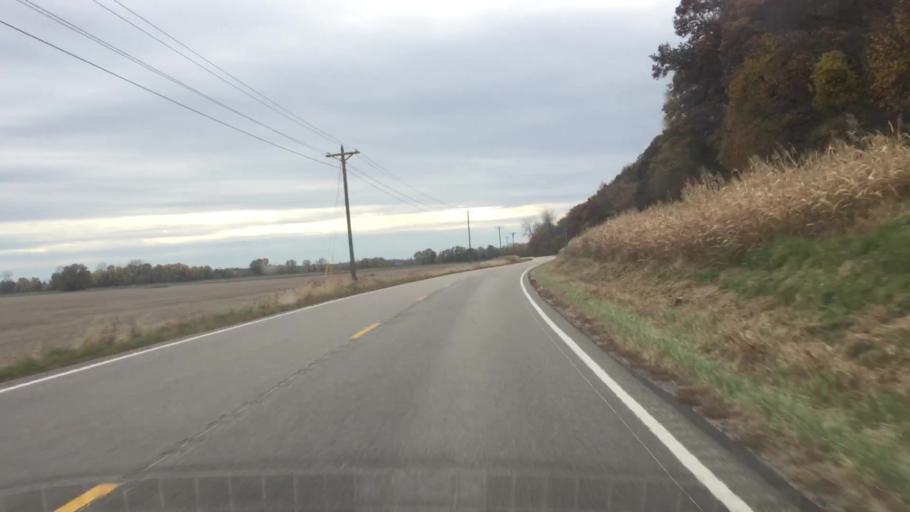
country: US
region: Missouri
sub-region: Callaway County
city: Holts Summit
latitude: 38.5844
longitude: -92.0497
